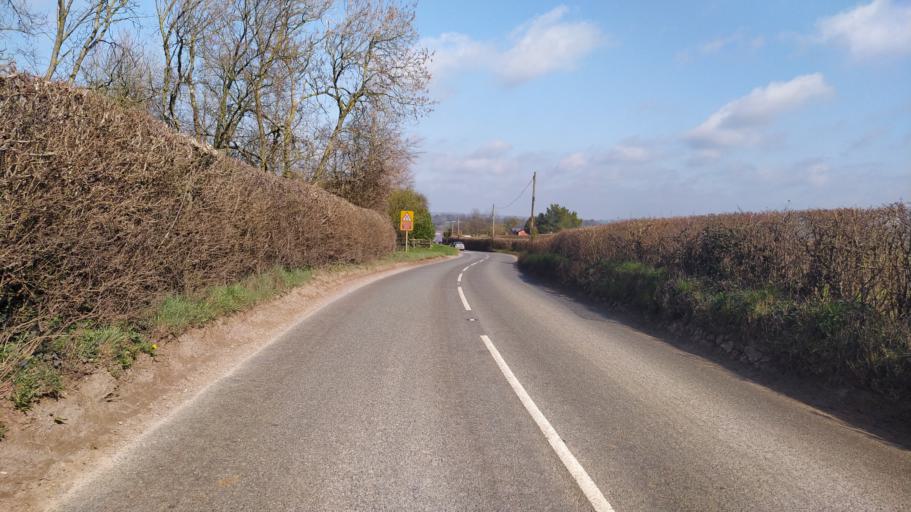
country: GB
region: England
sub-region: Somerset
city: Crewkerne
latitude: 50.8635
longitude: -2.7693
